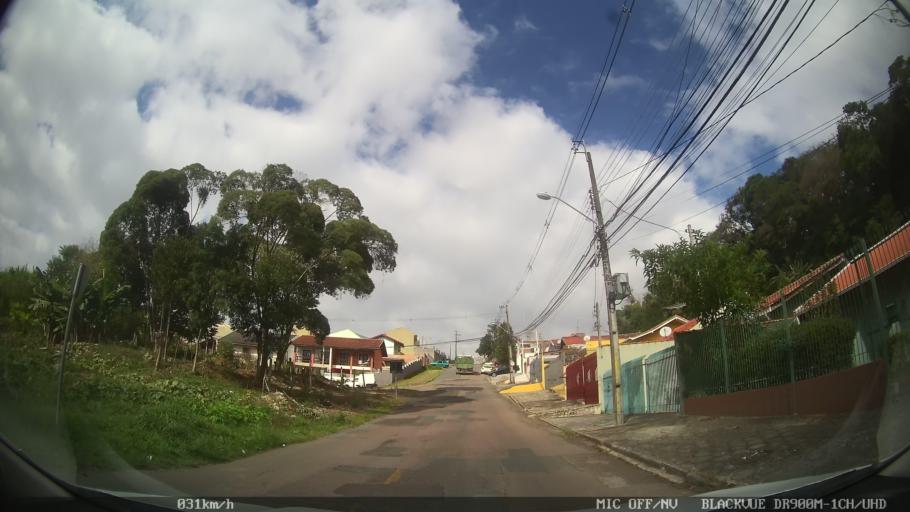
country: BR
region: Parana
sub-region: Curitiba
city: Curitiba
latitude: -25.3726
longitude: -49.2558
